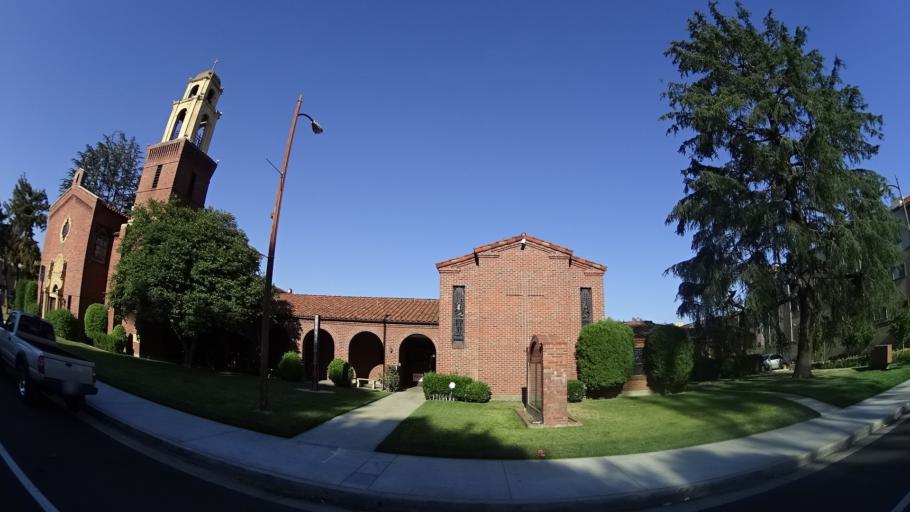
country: US
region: California
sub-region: Los Angeles County
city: North Hollywood
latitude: 34.1588
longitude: -118.3790
